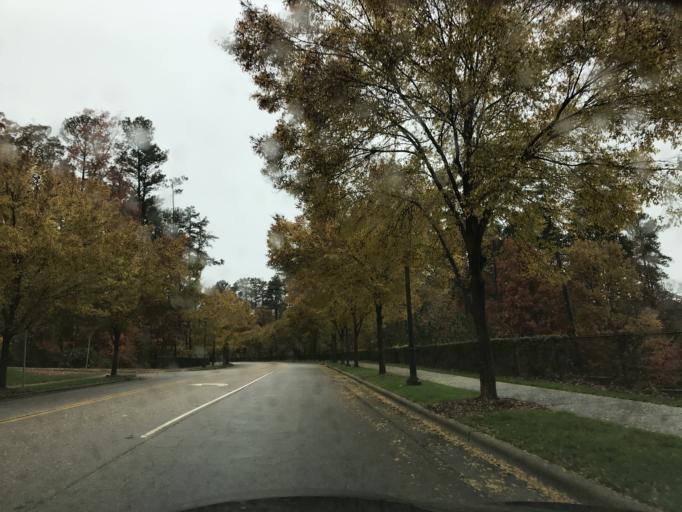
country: US
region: North Carolina
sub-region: Wake County
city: West Raleigh
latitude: 35.8353
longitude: -78.6324
